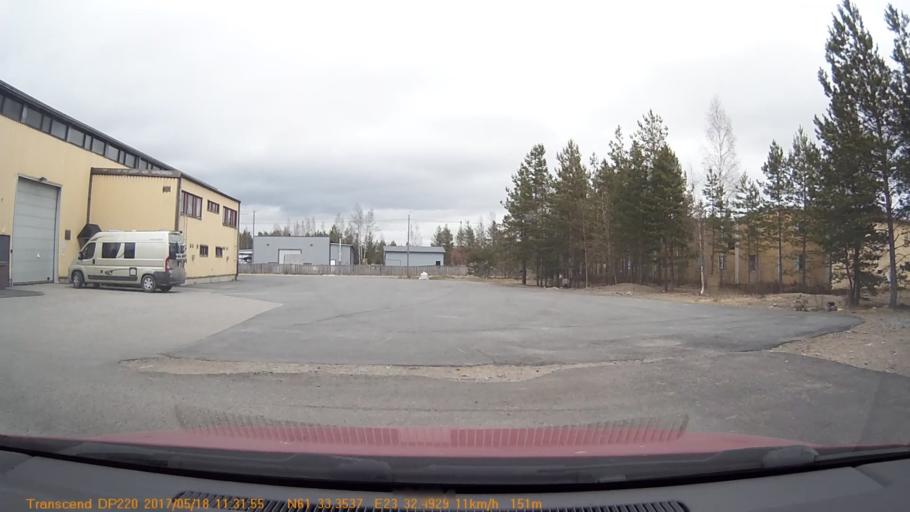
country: FI
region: Pirkanmaa
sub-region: Tampere
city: Yloejaervi
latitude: 61.5559
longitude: 23.5416
